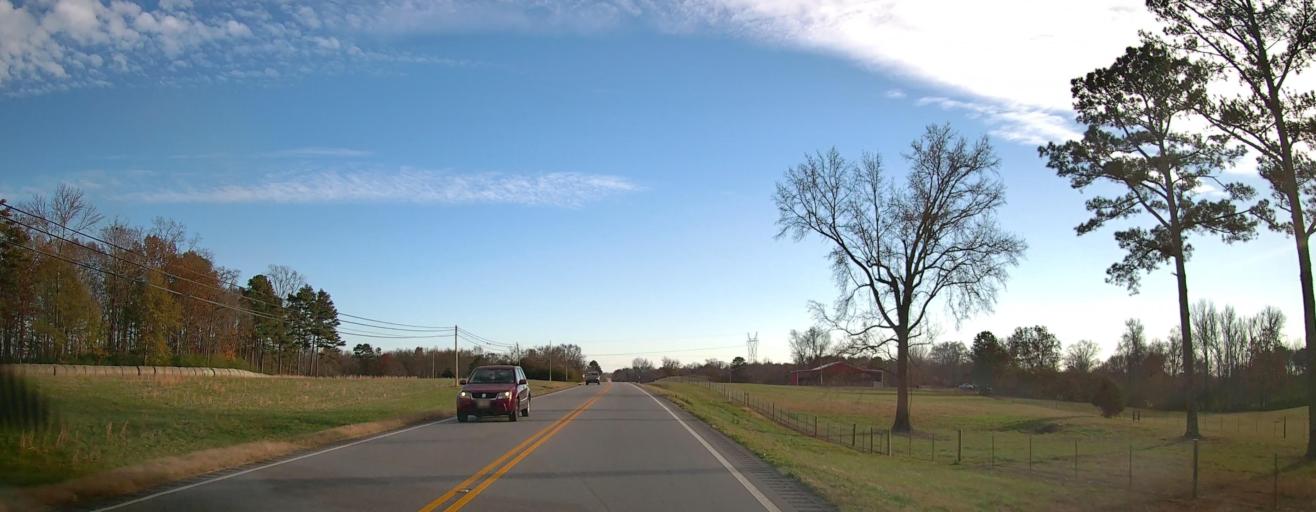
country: US
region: Alabama
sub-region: Marshall County
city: Arab
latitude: 34.3366
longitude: -86.6084
